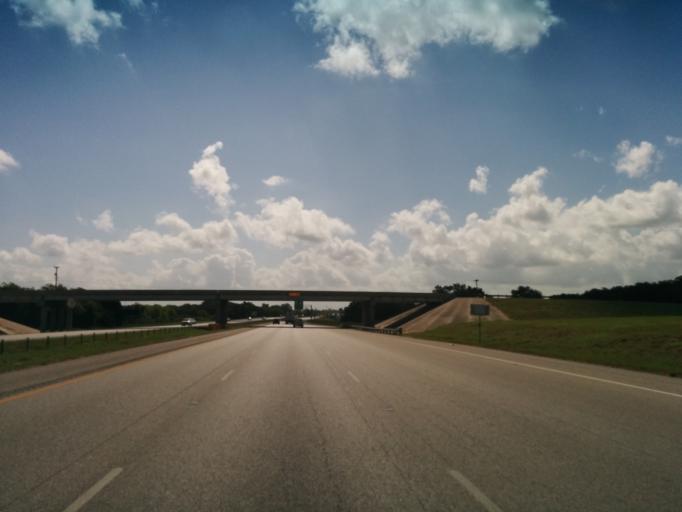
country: US
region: Texas
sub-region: Colorado County
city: Columbus
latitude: 29.6936
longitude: -96.5638
